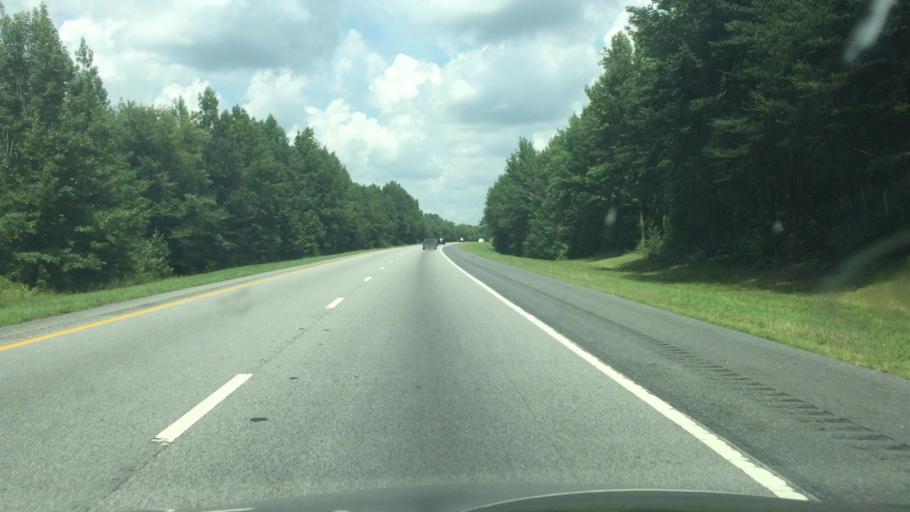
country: US
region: North Carolina
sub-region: Guilford County
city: Pleasant Garden
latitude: 35.9352
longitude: -79.8270
